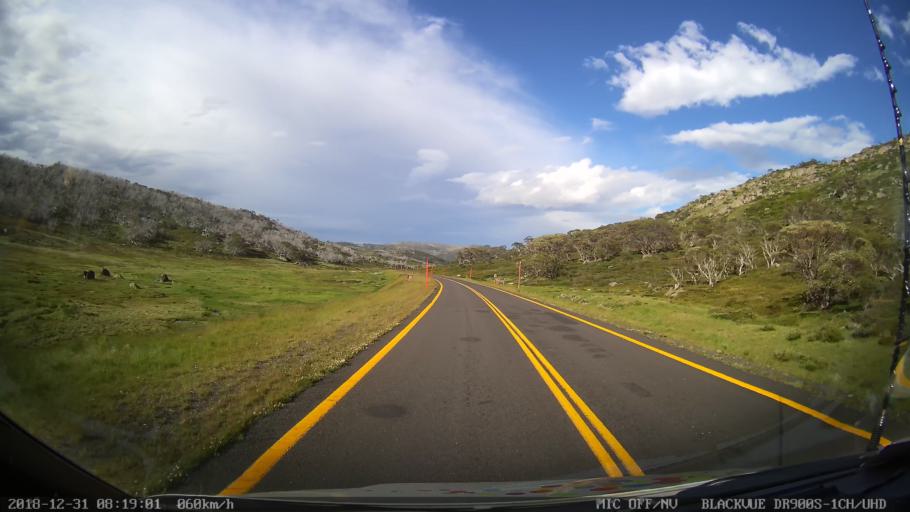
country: AU
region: New South Wales
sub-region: Snowy River
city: Jindabyne
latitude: -36.4169
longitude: 148.3905
